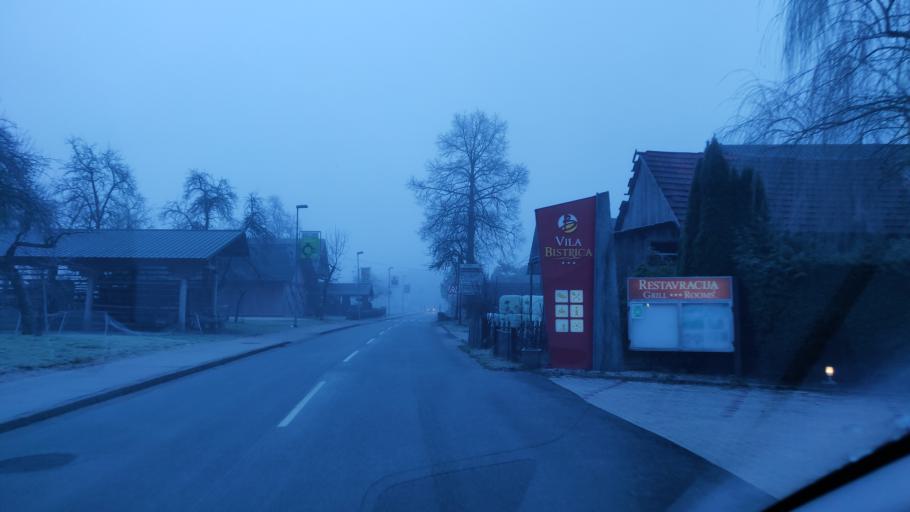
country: SI
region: Bohinj
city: Bohinjska Bistrica
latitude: 46.2749
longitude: 13.9520
